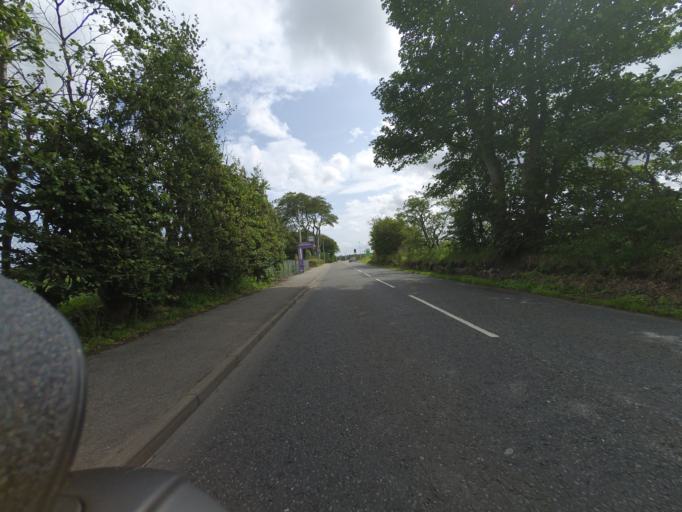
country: GB
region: Scotland
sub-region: Highland
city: Tain
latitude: 57.8057
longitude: -4.0471
